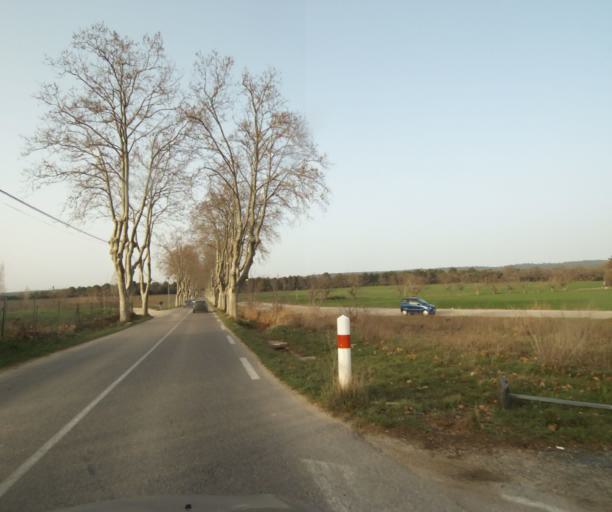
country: FR
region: Provence-Alpes-Cote d'Azur
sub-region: Departement des Bouches-du-Rhone
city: Eguilles
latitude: 43.6020
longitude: 5.3660
